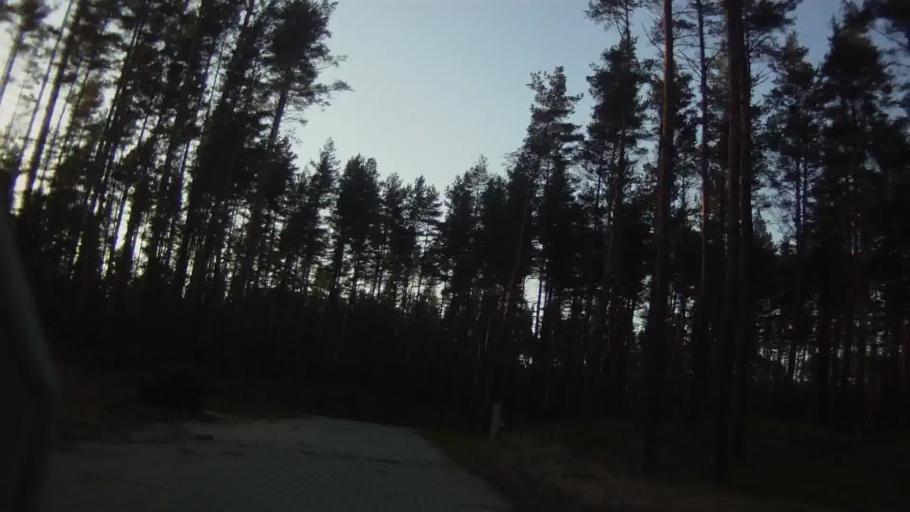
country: LV
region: Riga
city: Jaunciems
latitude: 57.0548
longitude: 24.1631
